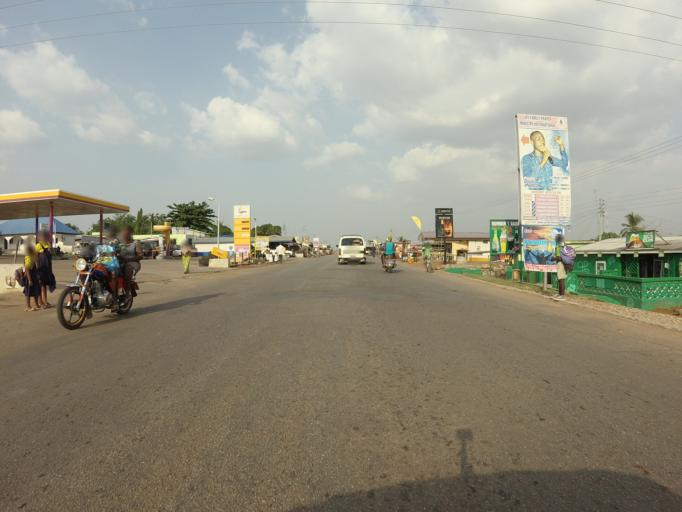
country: GH
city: Akropong
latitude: 6.2493
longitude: 0.1298
